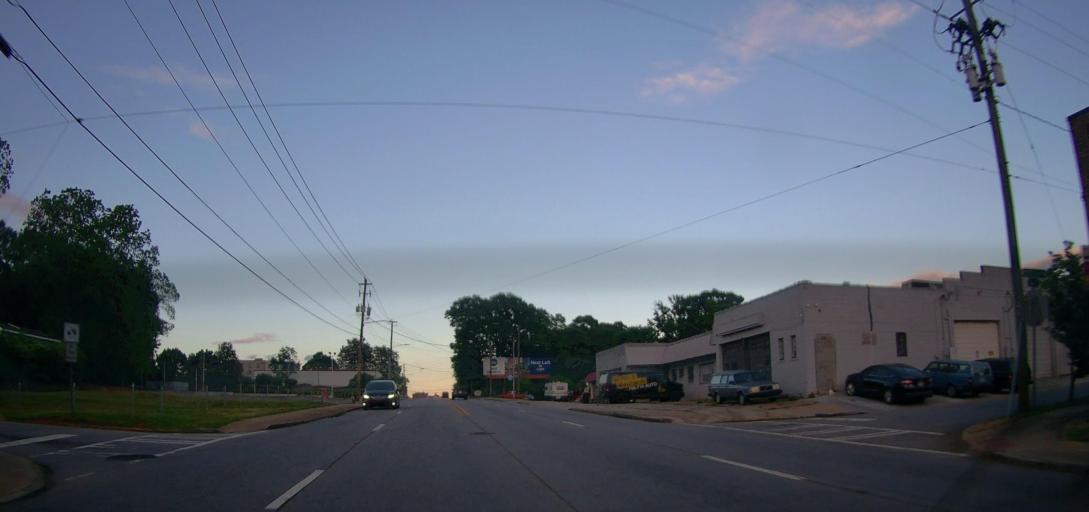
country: US
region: Georgia
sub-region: Clarke County
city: Athens
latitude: 33.9543
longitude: -83.3912
